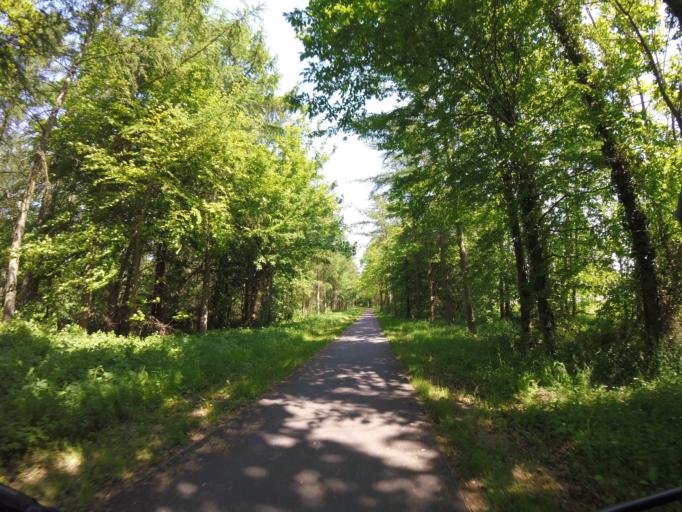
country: DE
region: Mecklenburg-Vorpommern
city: Bartenshagen-Parkentin
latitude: 54.1069
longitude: 11.9511
